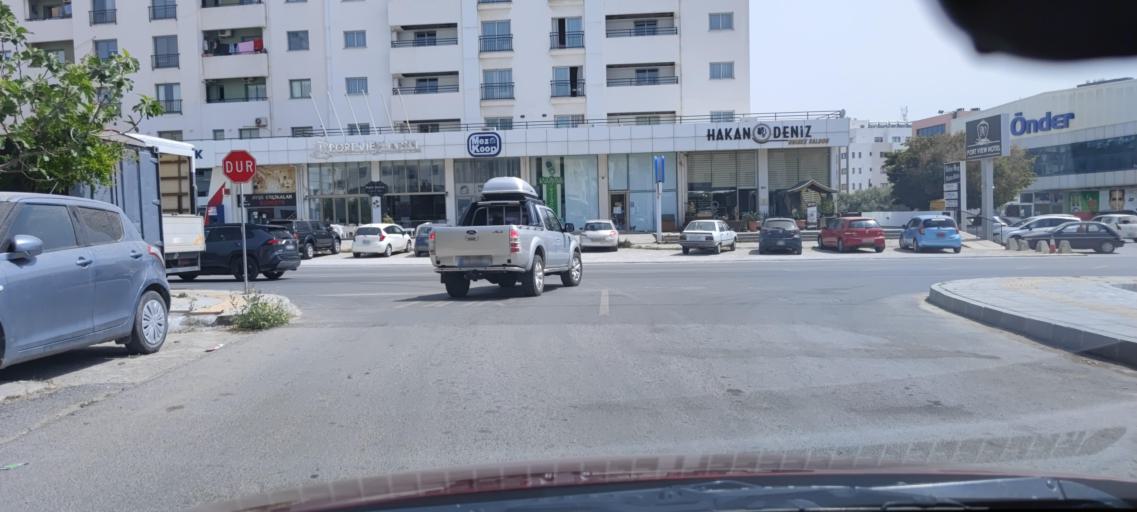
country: CY
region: Ammochostos
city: Famagusta
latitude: 35.1314
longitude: 33.9304
